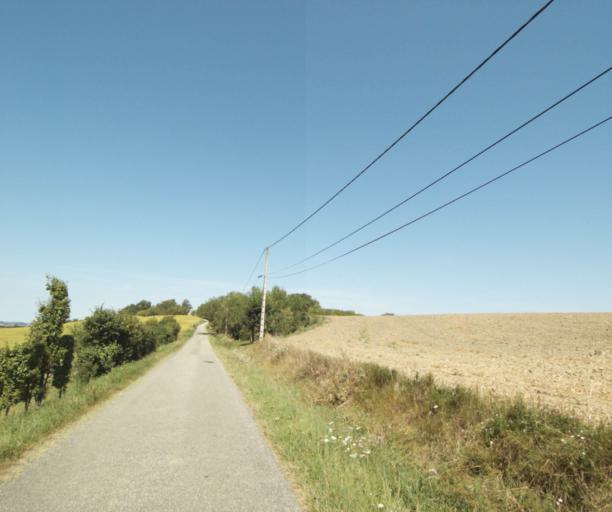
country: FR
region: Midi-Pyrenees
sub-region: Departement de l'Ariege
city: Lezat-sur-Leze
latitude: 43.2580
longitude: 1.3929
